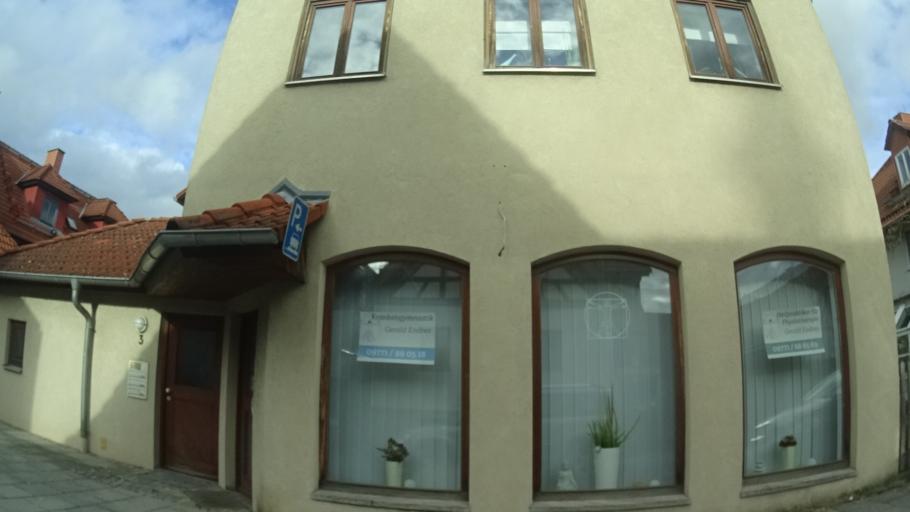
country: DE
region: Bavaria
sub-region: Regierungsbezirk Unterfranken
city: Heustreu
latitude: 50.3308
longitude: 10.2360
